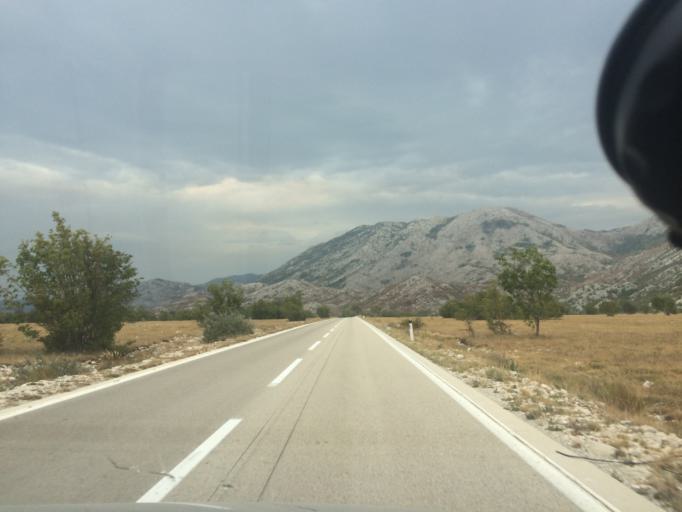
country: ME
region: Kotor
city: Risan
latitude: 42.5879
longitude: 18.6872
